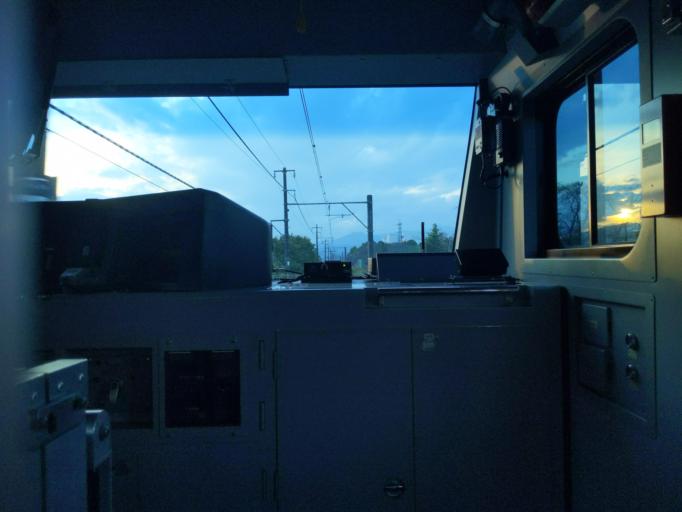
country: JP
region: Tokyo
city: Fussa
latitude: 35.7289
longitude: 139.2795
